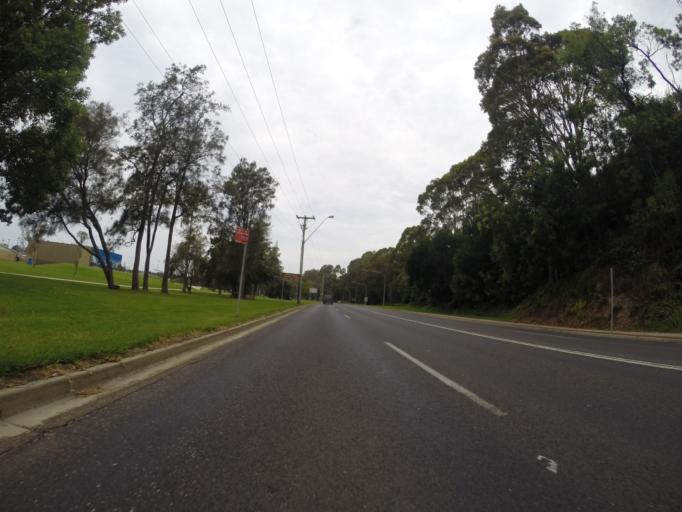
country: AU
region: New South Wales
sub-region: Eurobodalla
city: Batemans Bay
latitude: -35.7204
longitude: 150.1905
